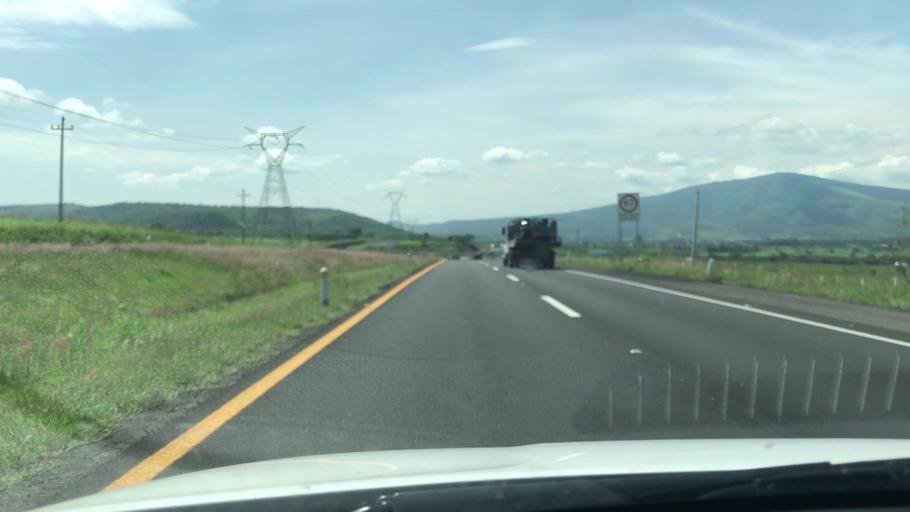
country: MX
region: Jalisco
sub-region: Zapotlanejo
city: La Mezquitera
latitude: 20.5901
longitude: -103.1041
